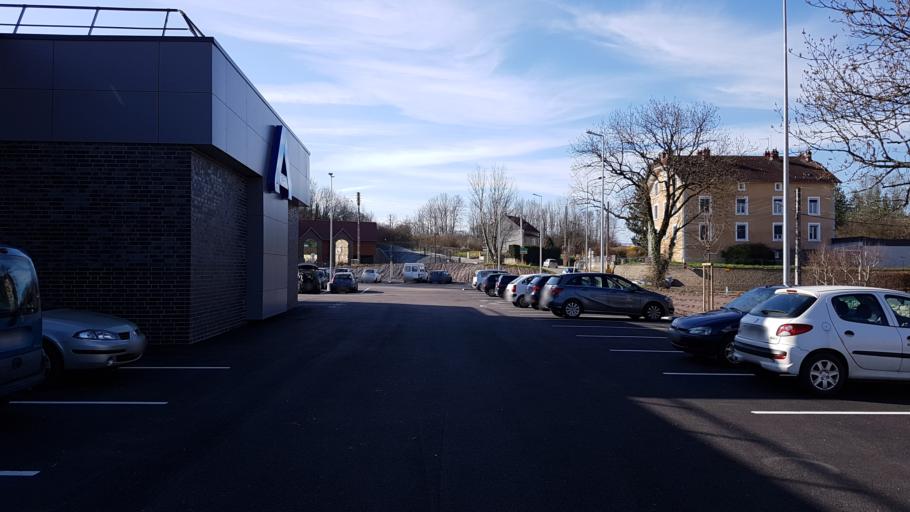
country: FR
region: Franche-Comte
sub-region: Departement du Jura
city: Montmorot
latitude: 46.6744
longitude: 5.5303
